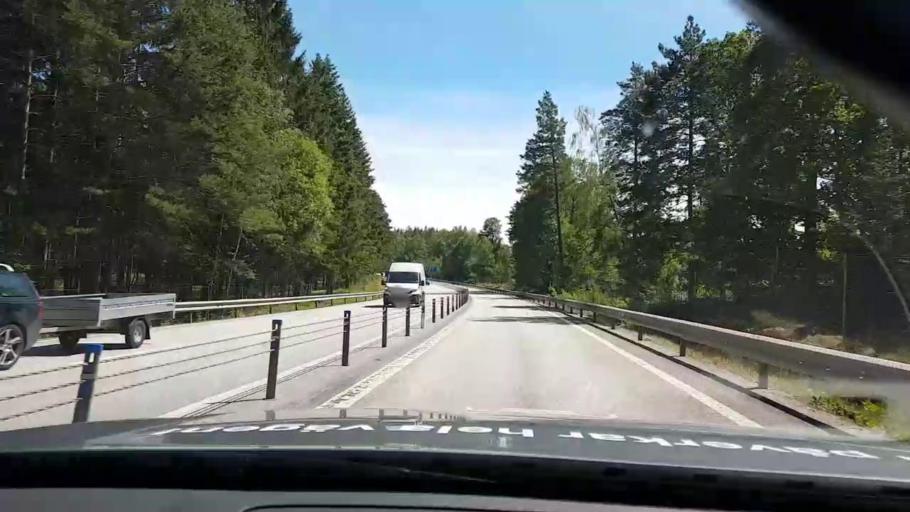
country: SE
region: Kalmar
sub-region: Vasterviks Kommun
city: Gamleby
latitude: 57.8284
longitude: 16.4458
